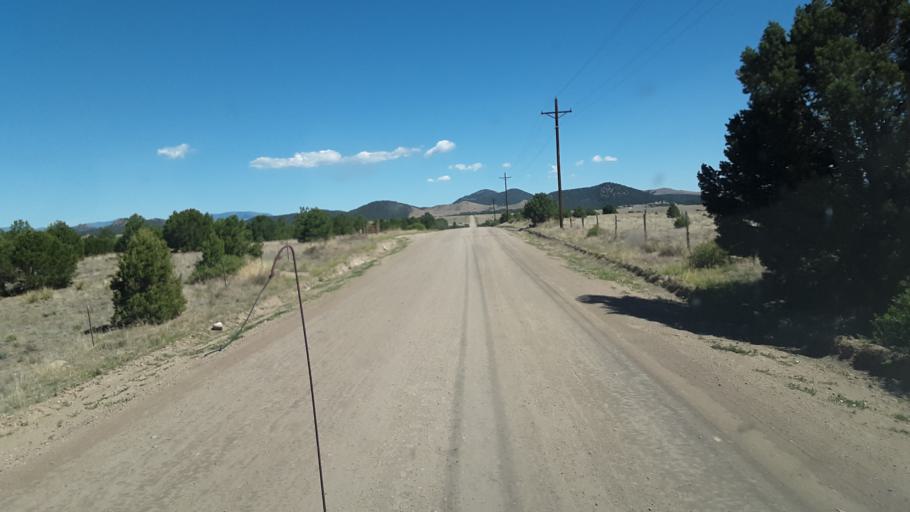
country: US
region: Colorado
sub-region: Custer County
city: Westcliffe
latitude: 38.2675
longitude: -105.5011
